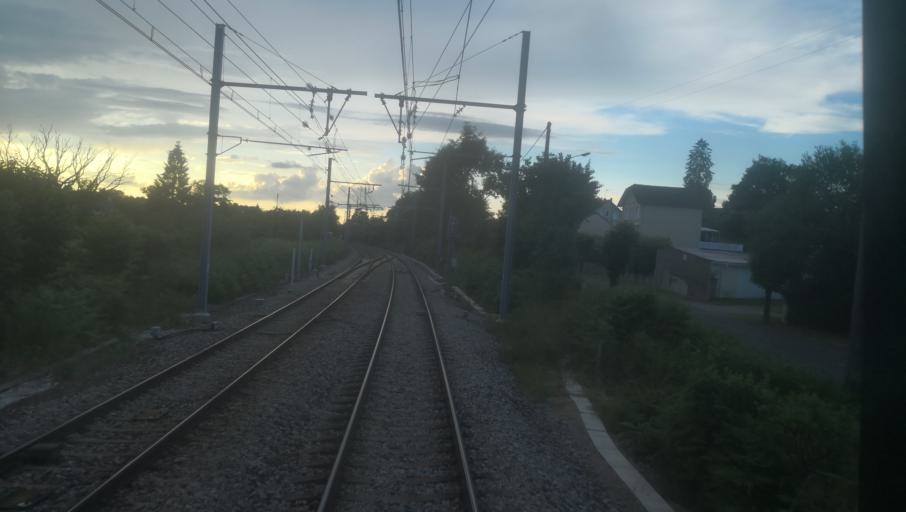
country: FR
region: Limousin
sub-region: Departement de la Creuse
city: La Souterraine
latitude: 46.2361
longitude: 1.4951
